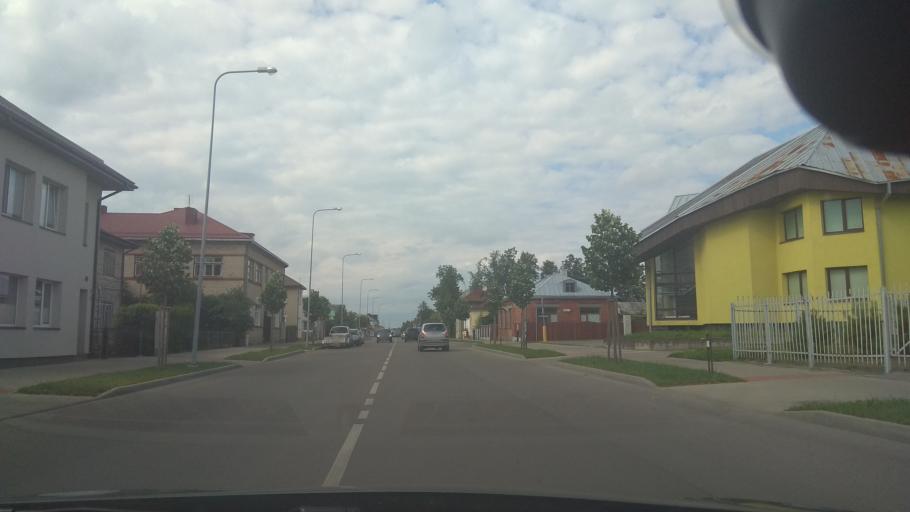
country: LT
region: Marijampoles apskritis
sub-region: Marijampole Municipality
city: Marijampole
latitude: 54.5516
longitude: 23.3534
